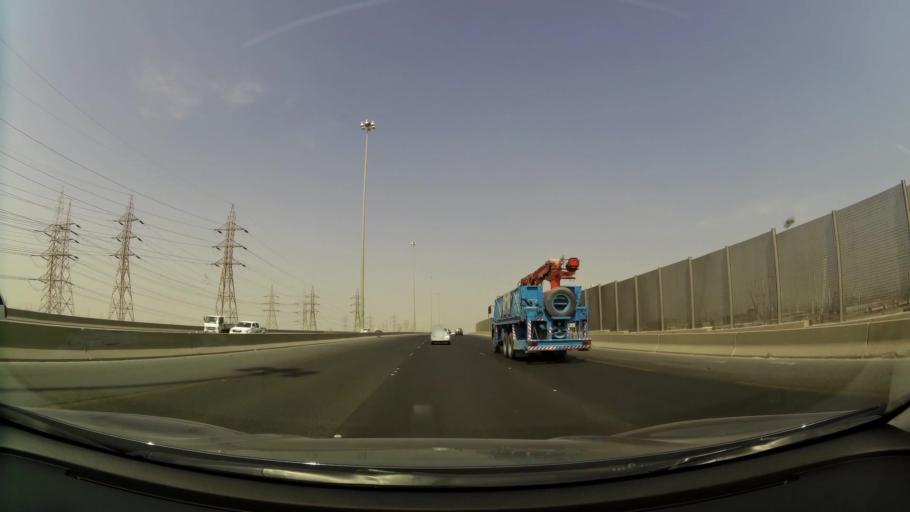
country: KW
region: Al Ahmadi
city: Al Fahahil
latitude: 29.0438
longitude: 48.1148
